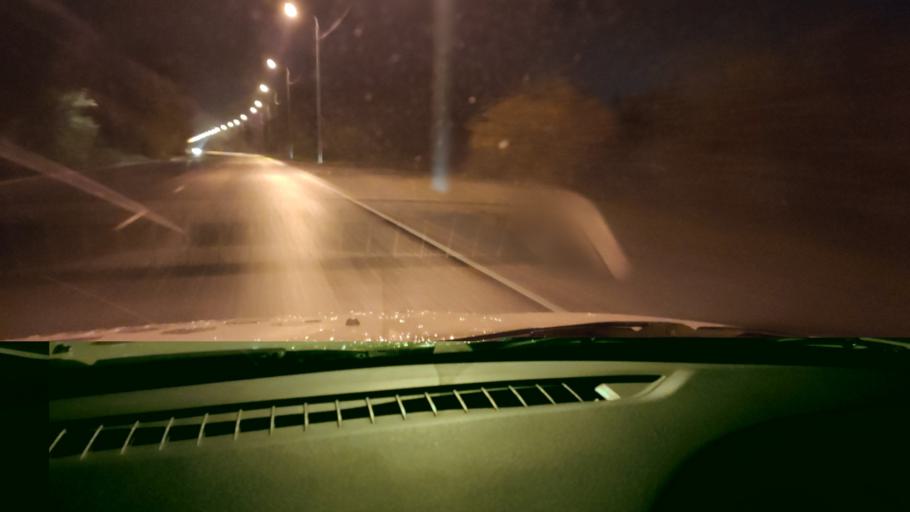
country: RU
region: Perm
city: Kondratovo
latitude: 57.9874
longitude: 56.1341
